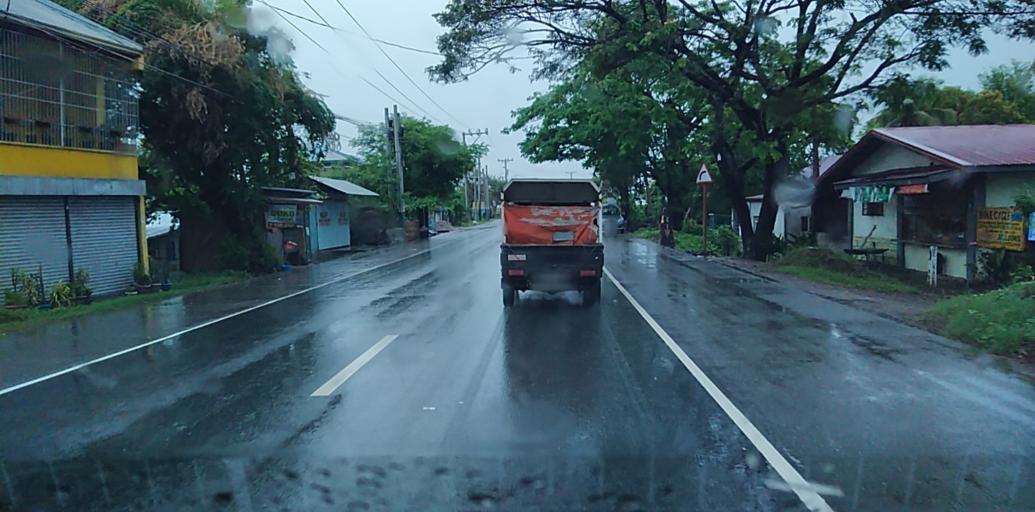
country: PH
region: Central Luzon
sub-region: Province of Bulacan
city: Bulualto
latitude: 15.2187
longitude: 120.9545
